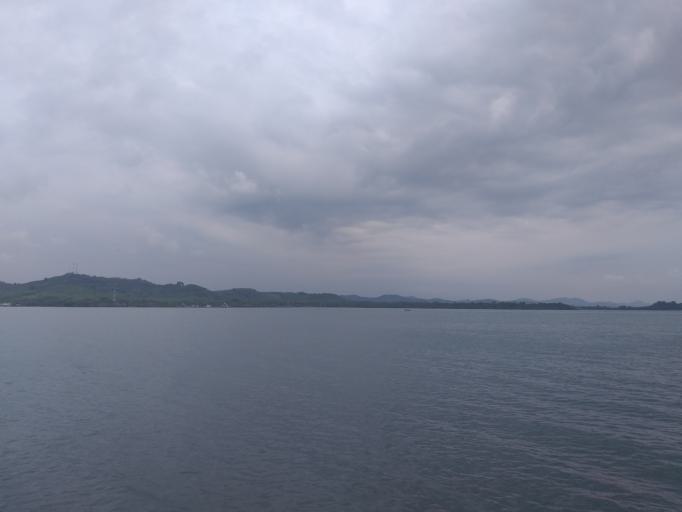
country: TH
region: Trat
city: Laem Ngop
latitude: 12.1681
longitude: 102.2958
